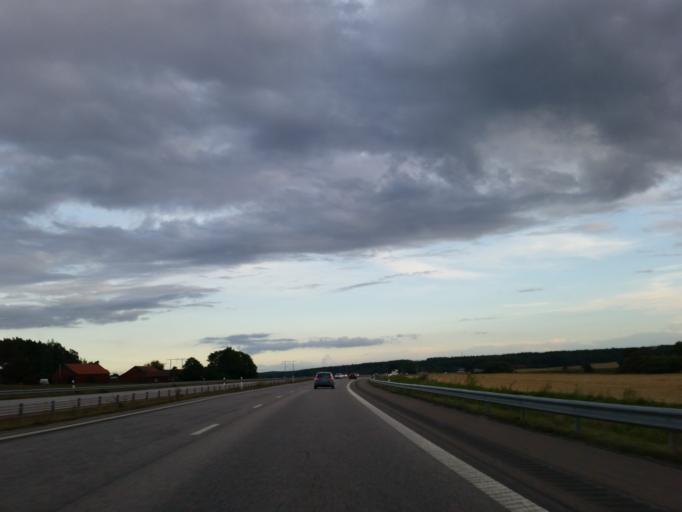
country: SE
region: Uppsala
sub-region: Uppsala Kommun
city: Saevja
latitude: 59.8218
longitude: 17.7498
